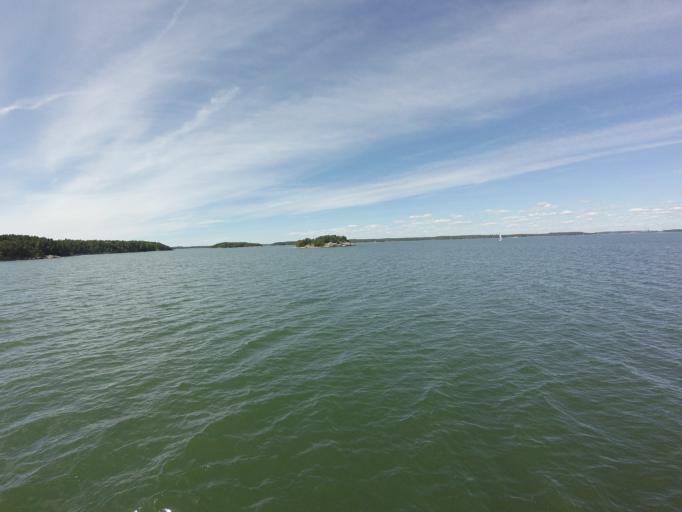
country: FI
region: Varsinais-Suomi
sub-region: Turku
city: Naantali
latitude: 60.3797
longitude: 22.0781
